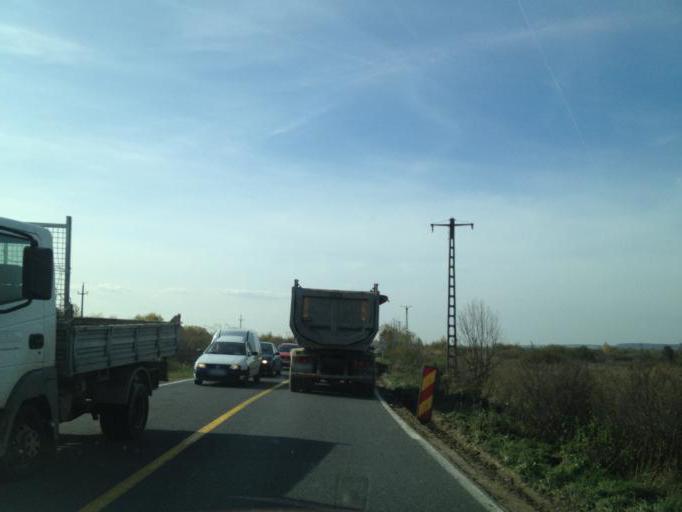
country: RO
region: Timis
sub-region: Comuna Margina
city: Margina
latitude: 45.8578
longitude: 22.2365
